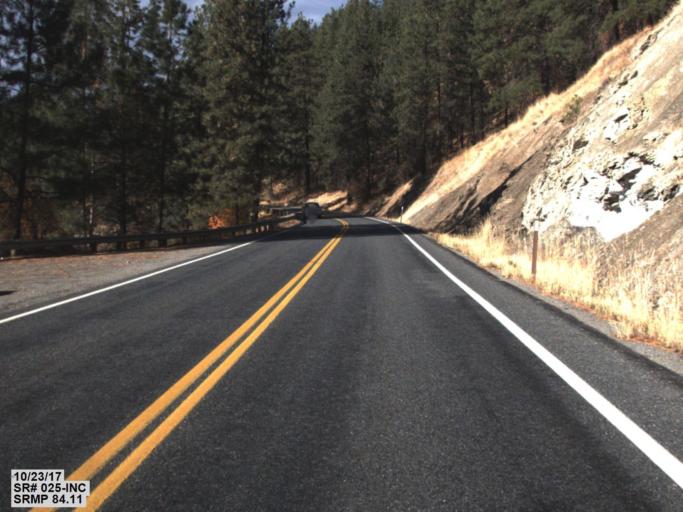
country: US
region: Washington
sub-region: Stevens County
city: Kettle Falls
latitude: 48.6454
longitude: -118.0803
